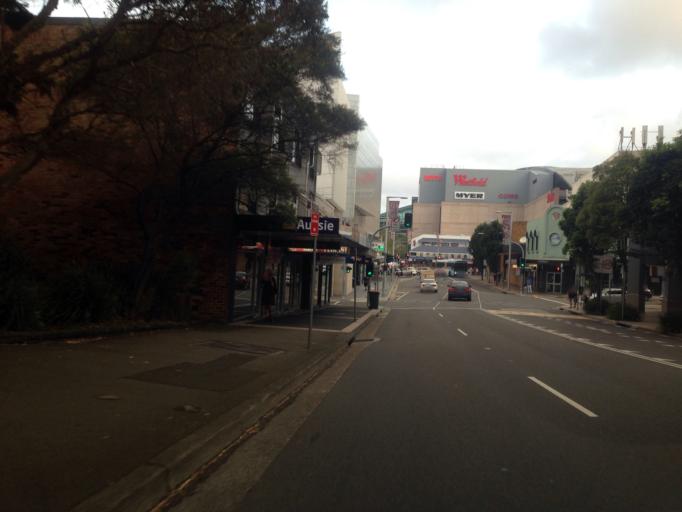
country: AU
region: New South Wales
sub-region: Willoughby
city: Chatswood
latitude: -33.7949
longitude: 151.1827
